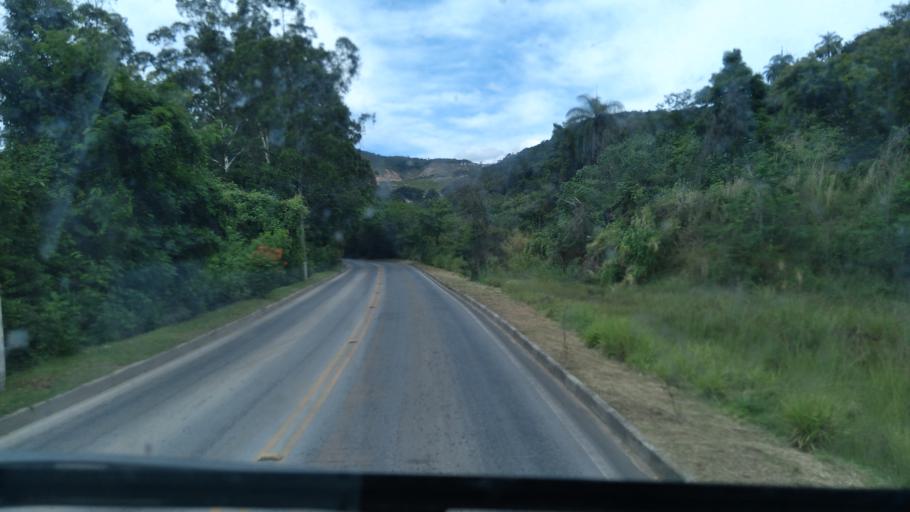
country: BR
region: Minas Gerais
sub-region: Santa Luzia
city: Santa Luzia
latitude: -19.8665
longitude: -43.8532
